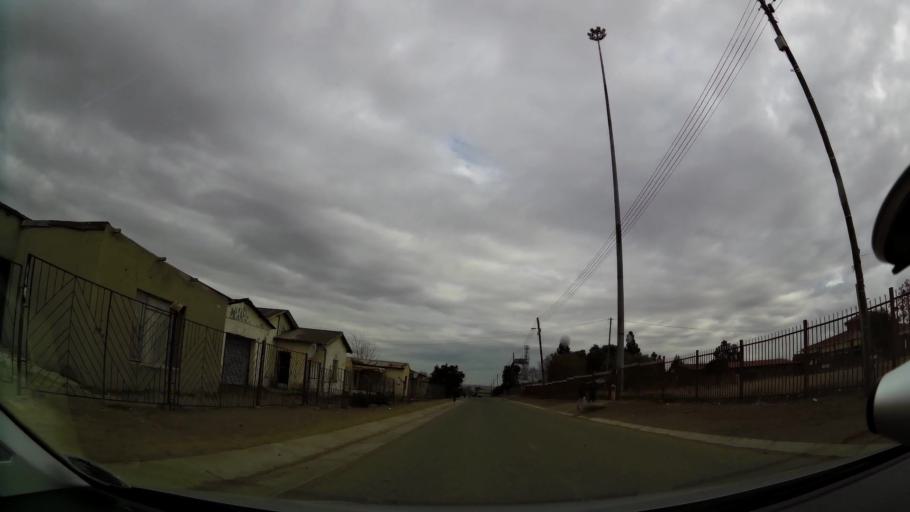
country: ZA
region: Orange Free State
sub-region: Fezile Dabi District Municipality
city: Kroonstad
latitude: -27.6480
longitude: 27.2046
